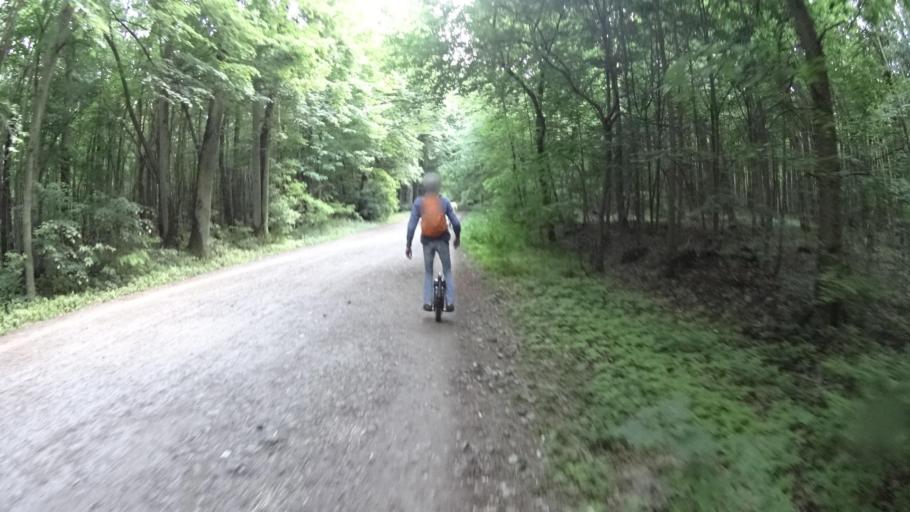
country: PL
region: Masovian Voivodeship
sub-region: Warszawa
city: Kabaty
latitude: 52.1230
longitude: 21.0838
